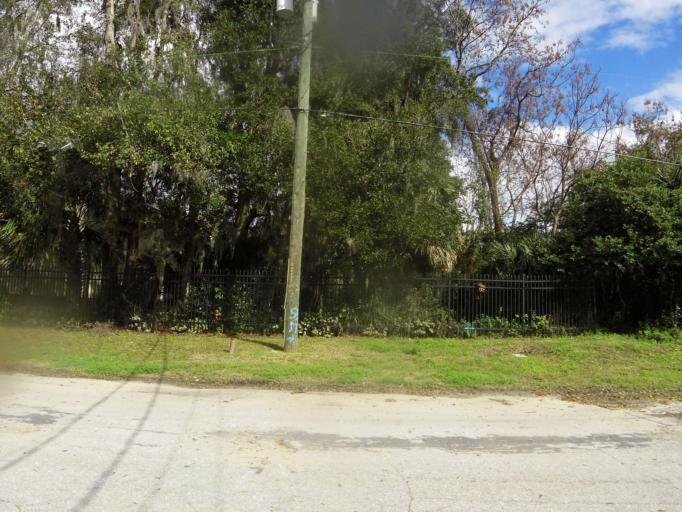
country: US
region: Florida
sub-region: Duval County
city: Jacksonville
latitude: 30.3297
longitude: -81.6016
